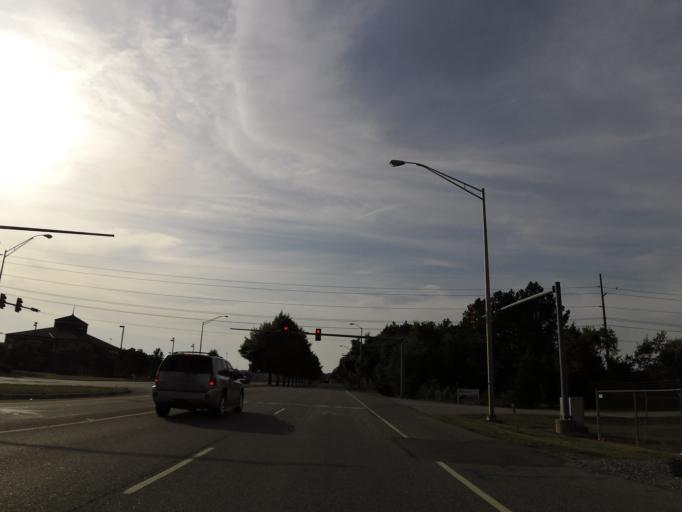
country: US
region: Tennessee
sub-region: Blount County
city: Alcoa
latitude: 35.7840
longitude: -83.9863
